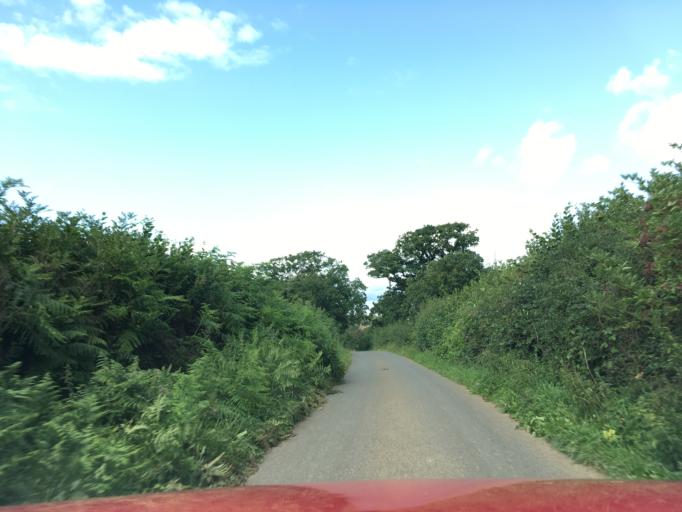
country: GB
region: England
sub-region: Wiltshire
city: Luckington
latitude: 51.6056
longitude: -2.2492
